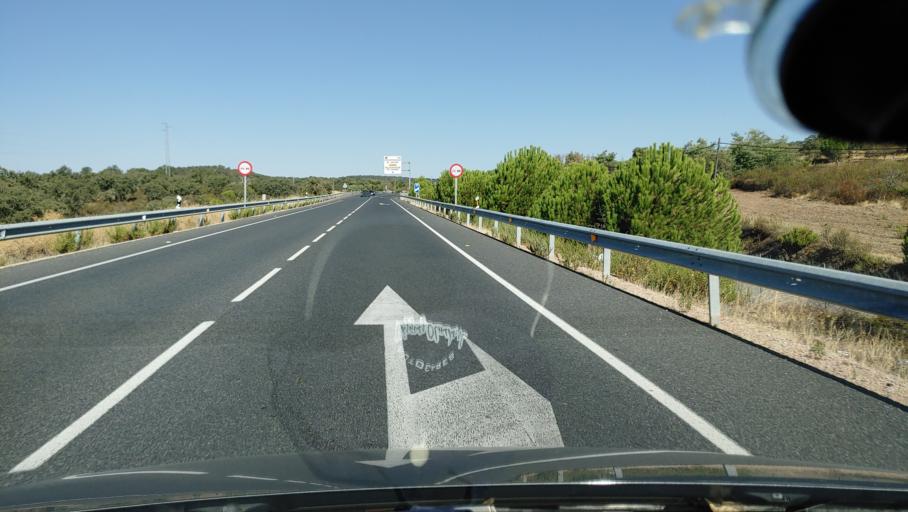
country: ES
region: Andalusia
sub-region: Province of Cordoba
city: Villaharta
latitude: 38.0924
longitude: -4.8669
